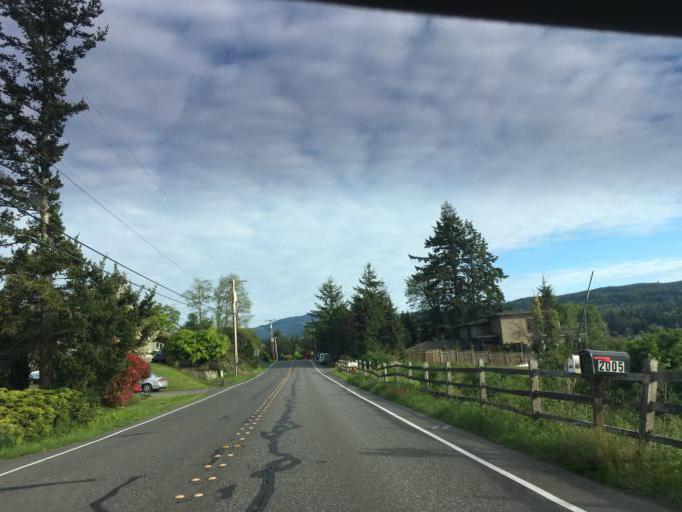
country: US
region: Washington
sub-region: Whatcom County
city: Geneva
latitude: 48.7602
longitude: -122.4005
